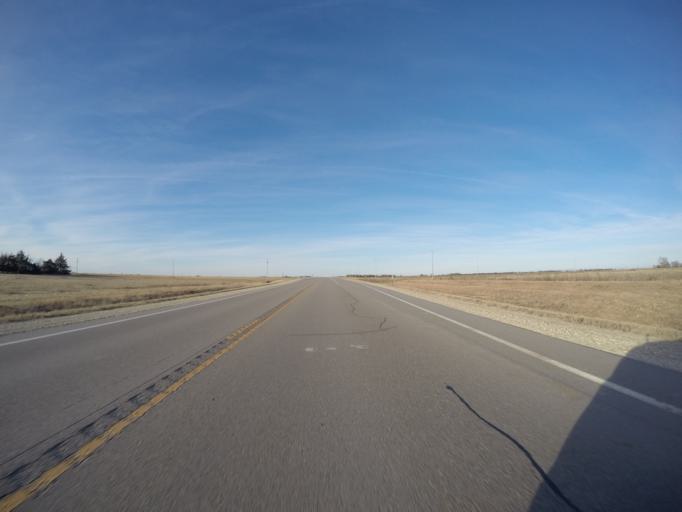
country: US
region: Kansas
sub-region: Marion County
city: Marion
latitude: 38.3180
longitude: -96.9666
